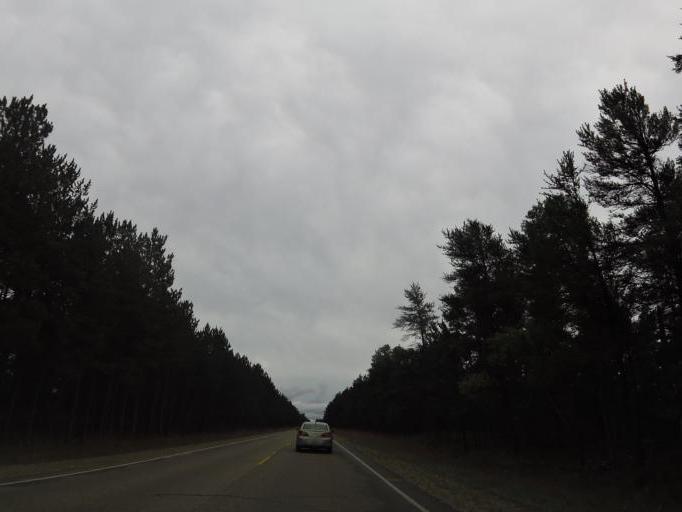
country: US
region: Michigan
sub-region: Roscommon County
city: Roscommon
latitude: 44.4810
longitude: -84.5628
